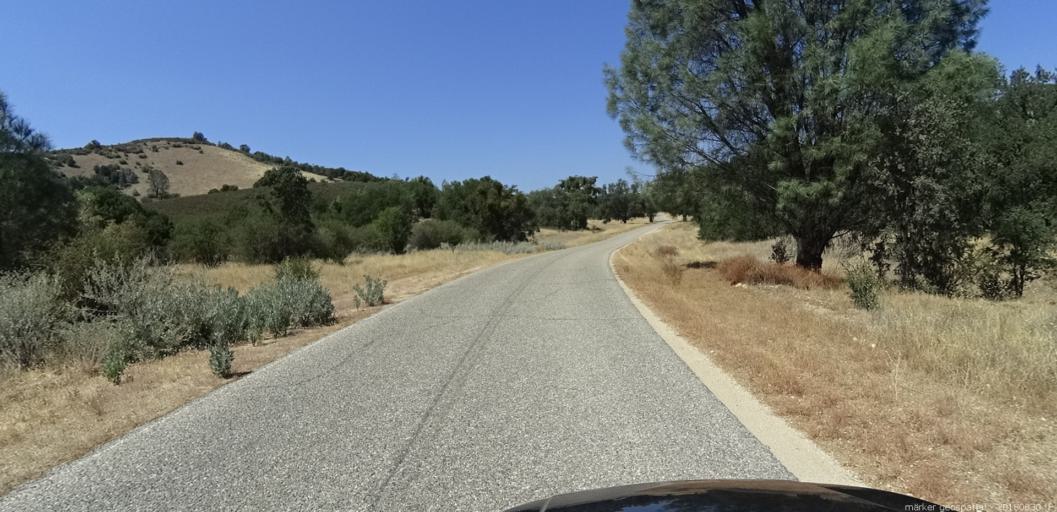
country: US
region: California
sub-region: Monterey County
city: King City
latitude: 36.0137
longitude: -121.2827
